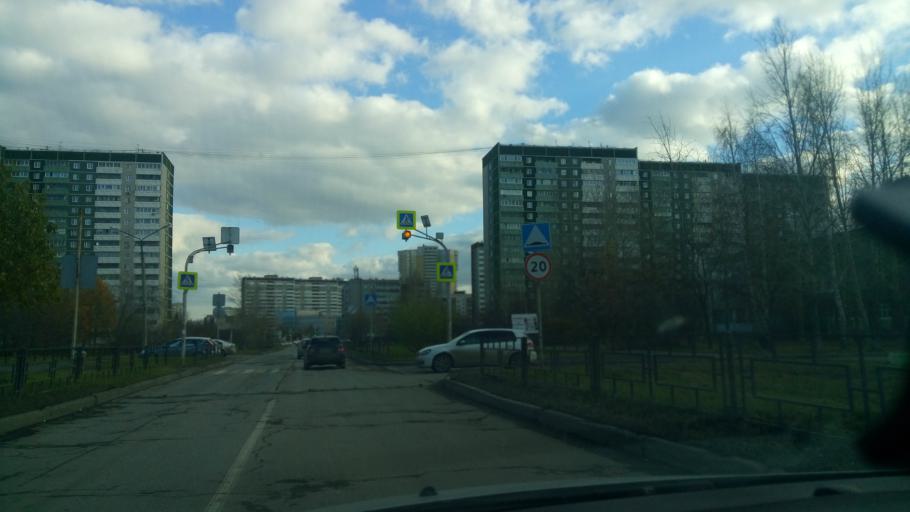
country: RU
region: Sverdlovsk
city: Yekaterinburg
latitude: 56.8666
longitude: 60.5392
